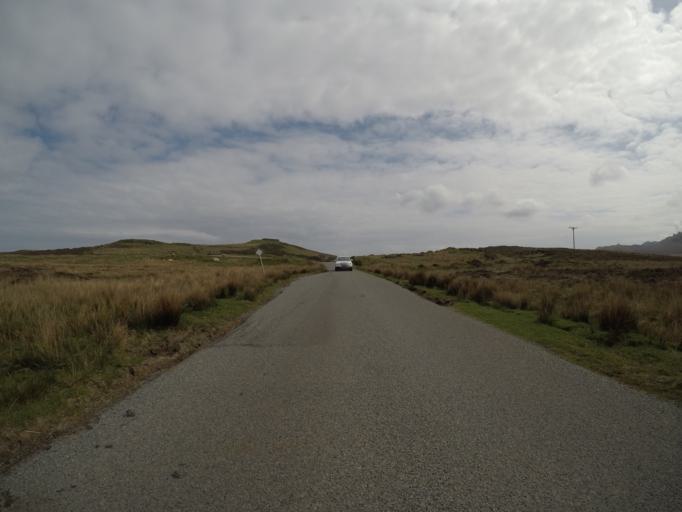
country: GB
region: Scotland
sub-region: Highland
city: Portree
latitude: 57.6812
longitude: -6.2829
